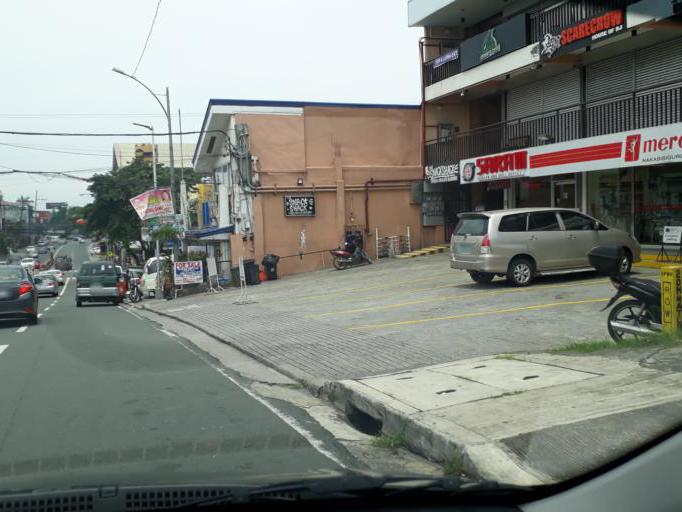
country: PH
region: Metro Manila
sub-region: Quezon City
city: Quezon City
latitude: 14.6359
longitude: 121.0594
